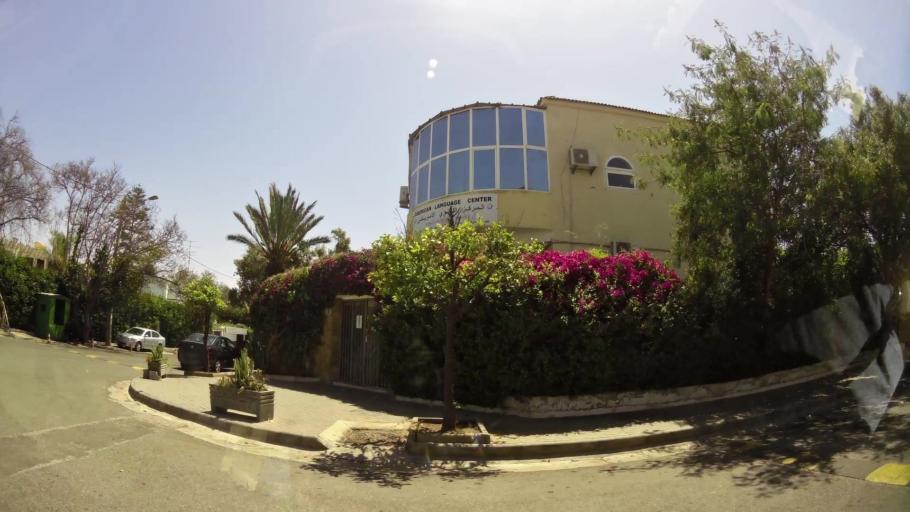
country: MA
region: Souss-Massa-Draa
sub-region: Agadir-Ida-ou-Tnan
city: Agadir
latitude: 30.4304
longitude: -9.5954
